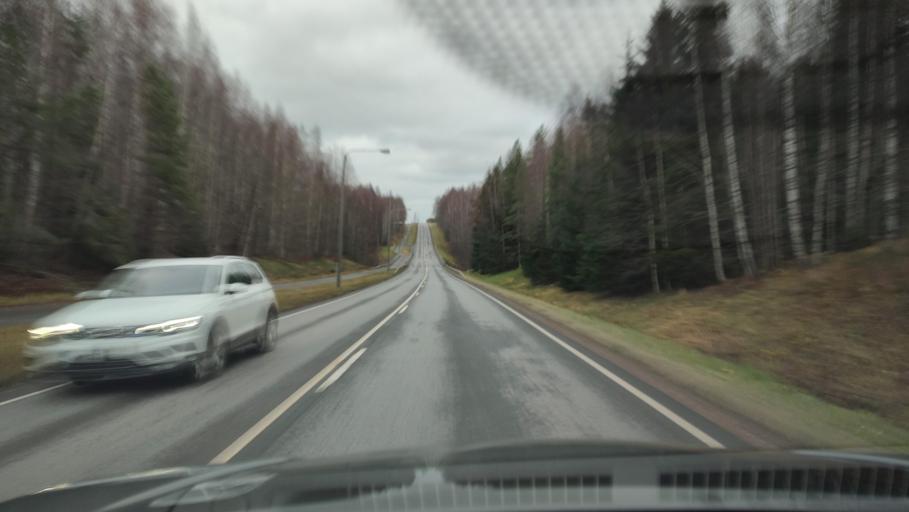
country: FI
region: Southern Ostrobothnia
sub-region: Seinaejoki
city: Kurikka
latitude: 62.5907
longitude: 22.4108
